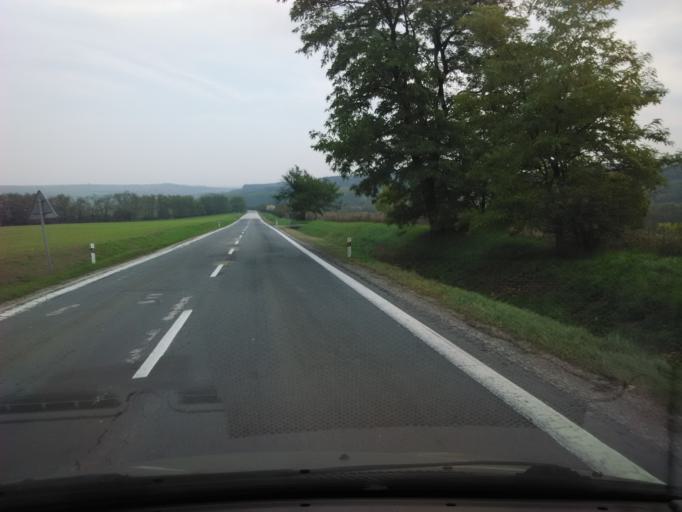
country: SK
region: Nitriansky
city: Svodin
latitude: 48.0368
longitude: 18.4368
